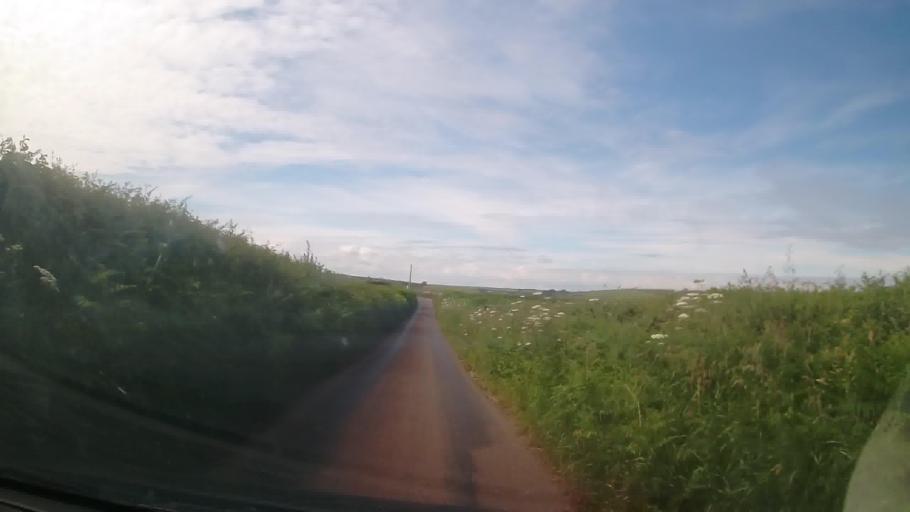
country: GB
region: England
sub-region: Devon
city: Salcombe
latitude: 50.2359
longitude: -3.6741
